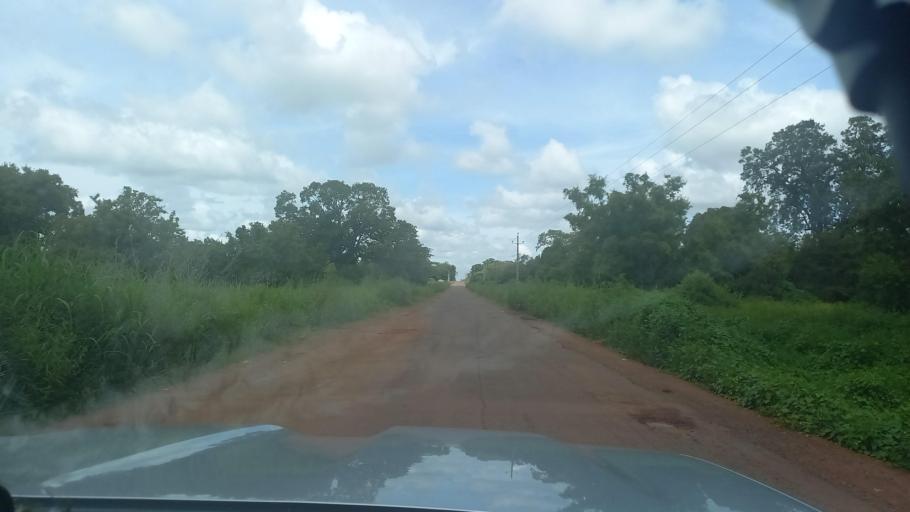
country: GM
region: Lower River
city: Kaiaf
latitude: 13.2166
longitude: -15.5434
